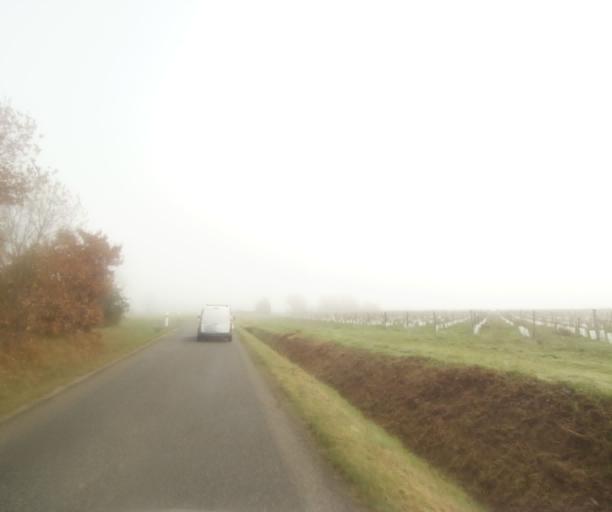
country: FR
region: Midi-Pyrenees
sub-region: Departement de la Haute-Garonne
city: Villaudric
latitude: 43.8345
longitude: 1.4585
